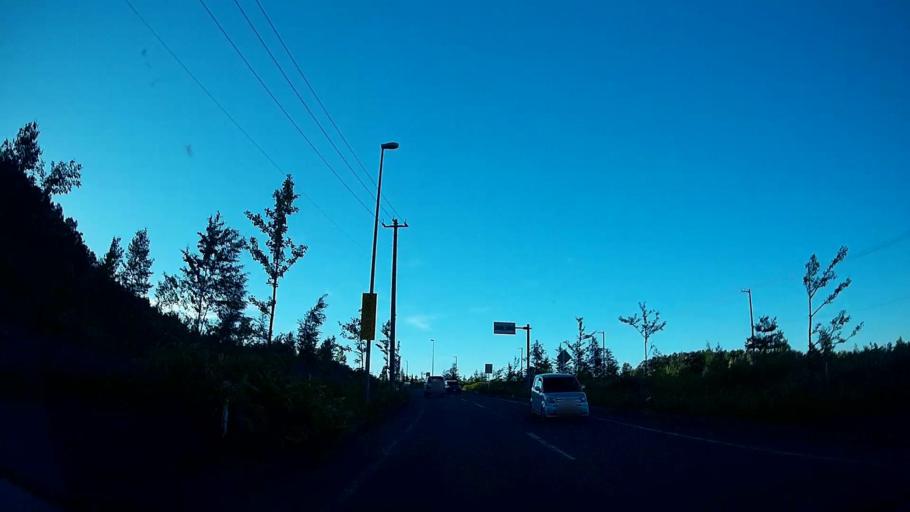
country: JP
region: Hokkaido
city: Otaru
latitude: 43.1649
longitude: 141.0238
